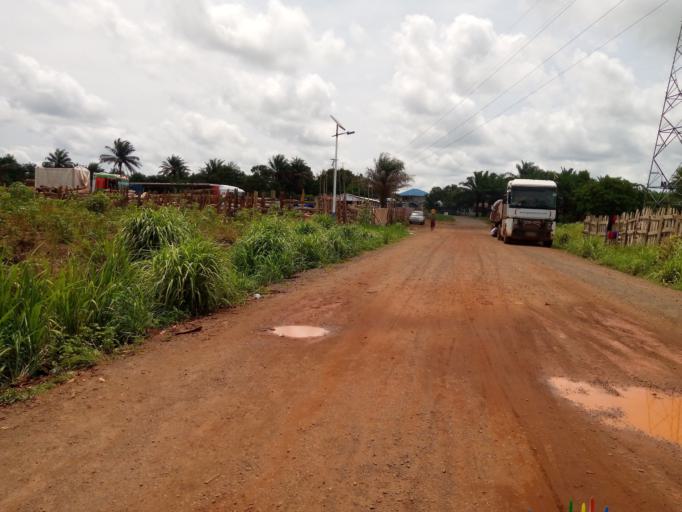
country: SL
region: Western Area
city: Waterloo
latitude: 8.3404
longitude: -12.9873
